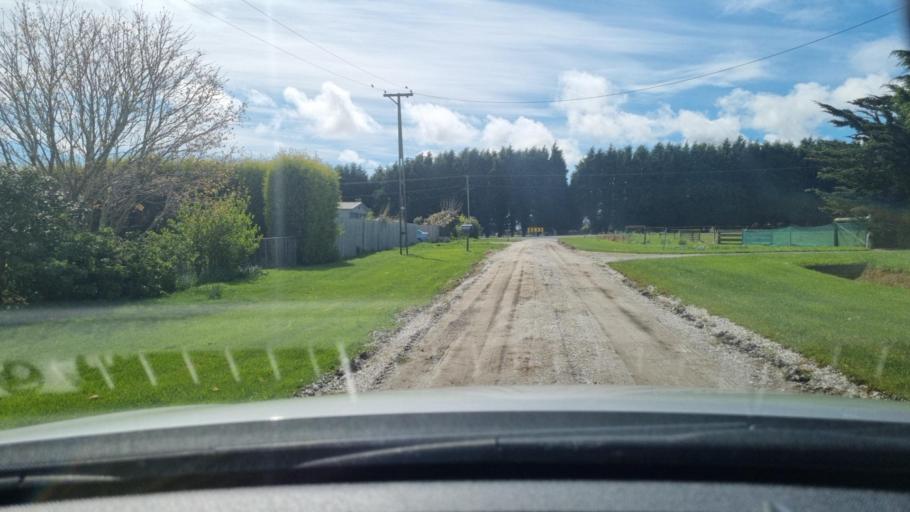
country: NZ
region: Southland
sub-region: Invercargill City
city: Invercargill
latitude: -46.4764
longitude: 168.3914
